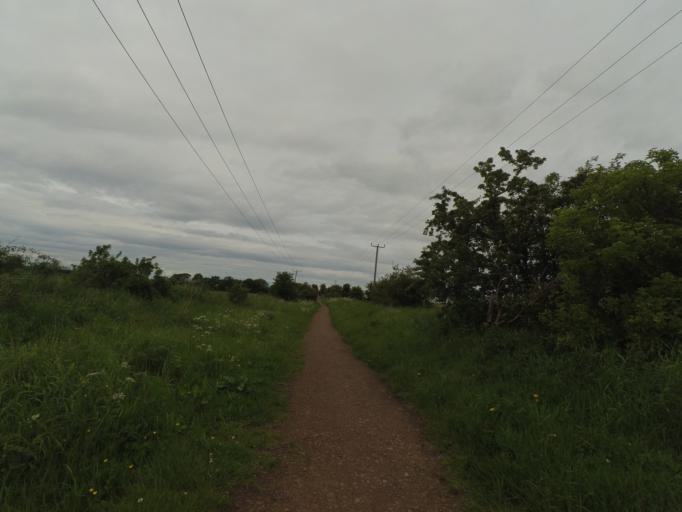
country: GB
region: Scotland
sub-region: East Lothian
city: Macmerry
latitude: 55.9348
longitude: -2.9115
